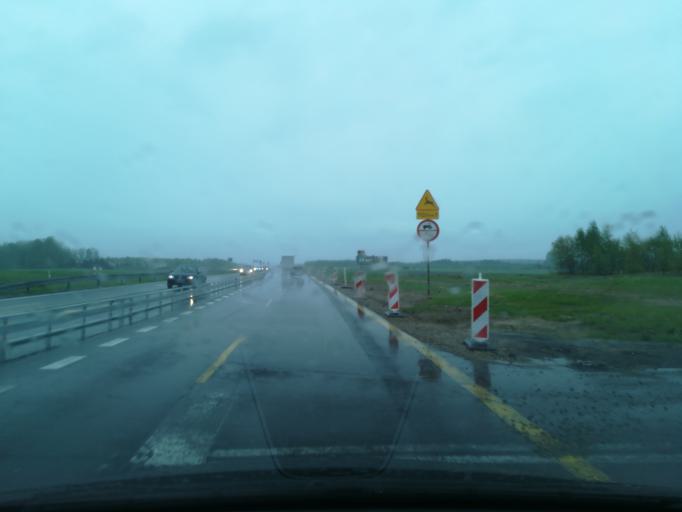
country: PL
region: Silesian Voivodeship
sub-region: Powiat czestochowski
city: Mykanow
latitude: 50.9238
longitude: 19.2242
